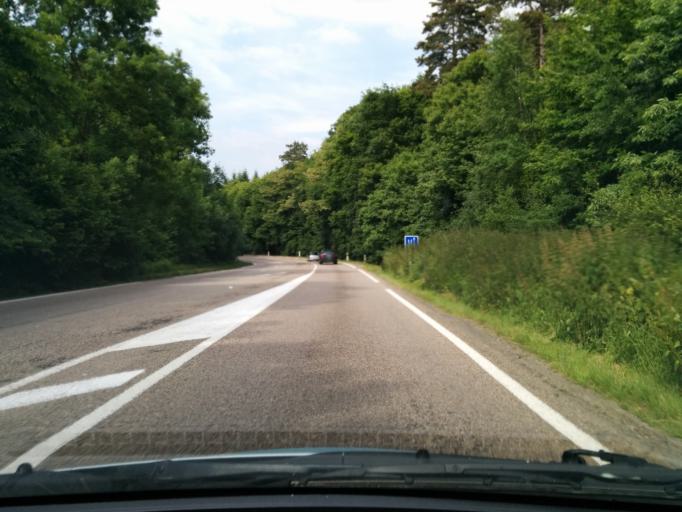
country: FR
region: Haute-Normandie
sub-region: Departement de l'Eure
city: Saint-Aubin-sur-Gaillon
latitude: 49.1413
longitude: 1.3184
